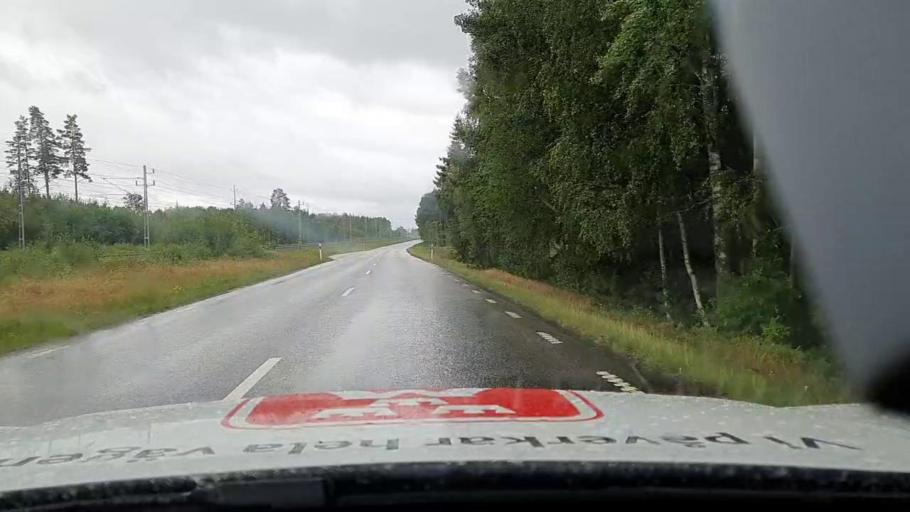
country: SE
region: Vaestra Goetaland
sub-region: Toreboda Kommun
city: Toereboda
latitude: 58.6644
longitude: 14.0904
